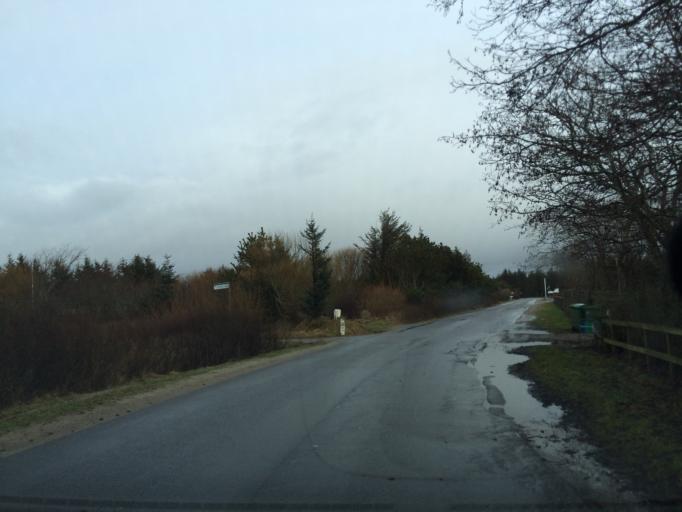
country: DK
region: Central Jutland
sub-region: Holstebro Kommune
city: Ulfborg
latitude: 56.2596
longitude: 8.1431
